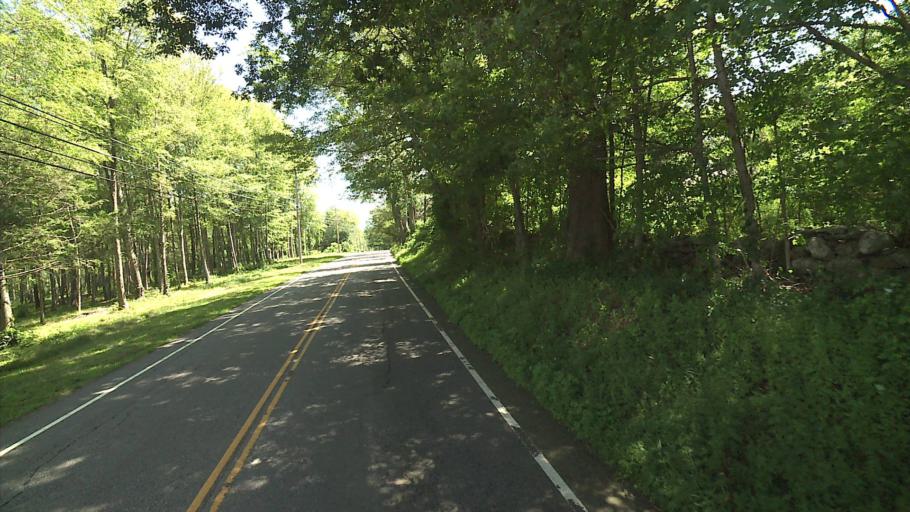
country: US
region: Connecticut
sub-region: Windham County
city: Windham
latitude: 41.7915
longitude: -72.0594
